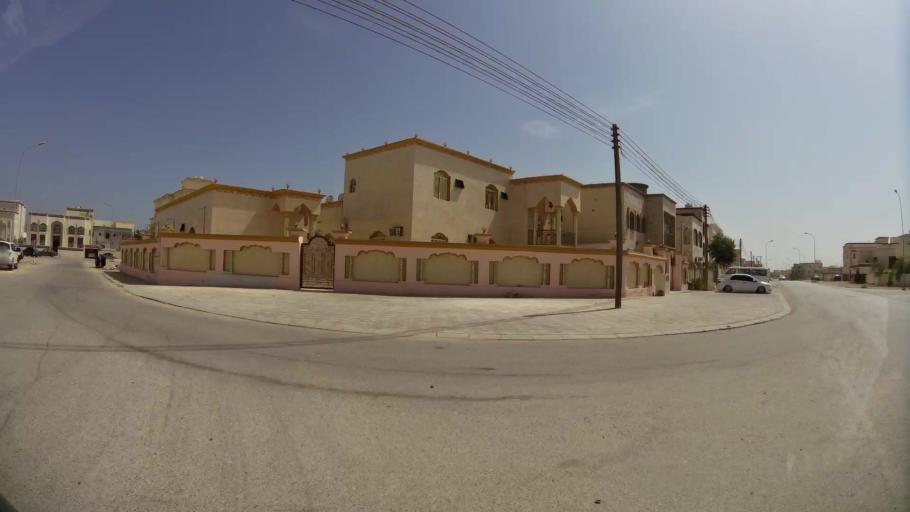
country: OM
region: Zufar
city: Salalah
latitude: 17.0415
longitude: 54.1592
